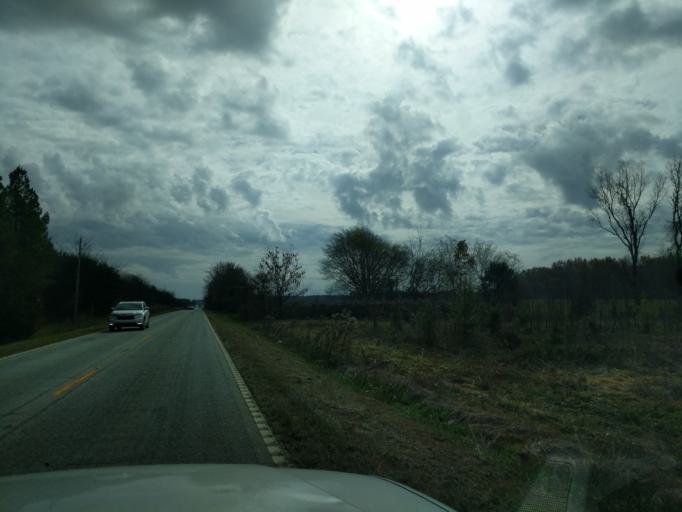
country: US
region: South Carolina
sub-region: Laurens County
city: Joanna
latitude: 34.4045
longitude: -81.8573
